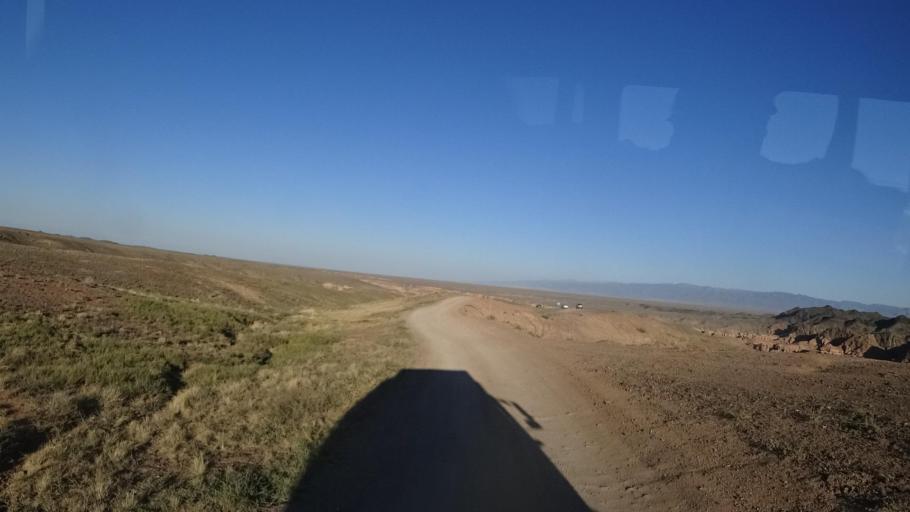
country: KZ
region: Almaty Oblysy
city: Kegen
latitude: 43.3551
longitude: 79.0638
